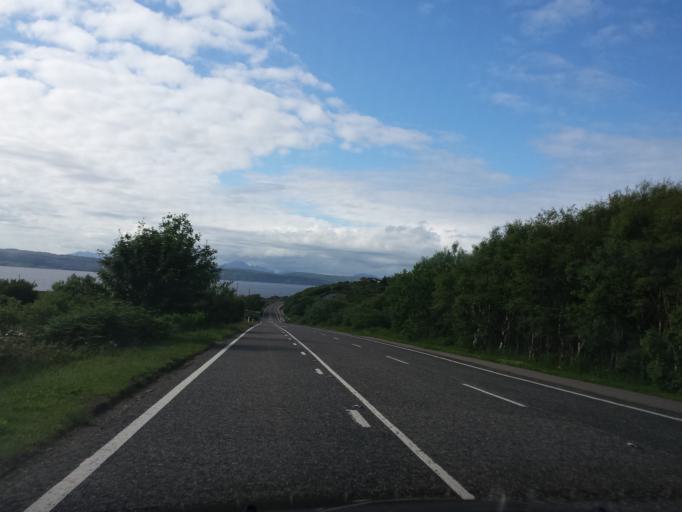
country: GB
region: Scotland
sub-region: Argyll and Bute
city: Isle Of Mull
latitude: 56.9906
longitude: -5.8269
